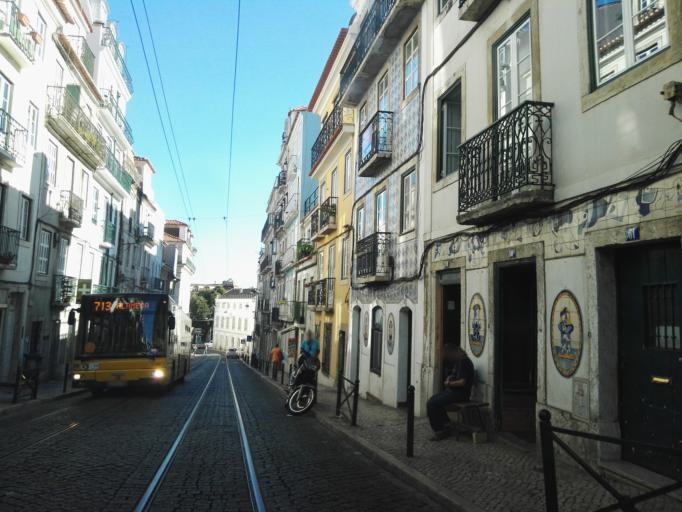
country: PT
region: Setubal
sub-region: Almada
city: Cacilhas
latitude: 38.7077
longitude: -9.1585
